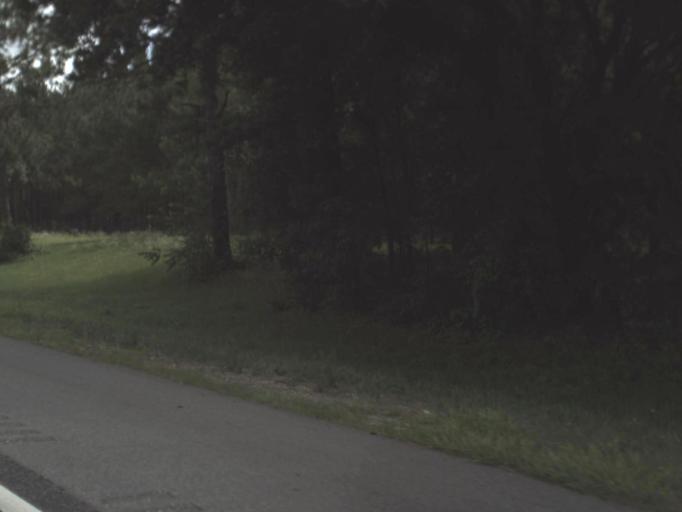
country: US
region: Florida
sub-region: Columbia County
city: Watertown
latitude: 30.0140
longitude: -82.6070
